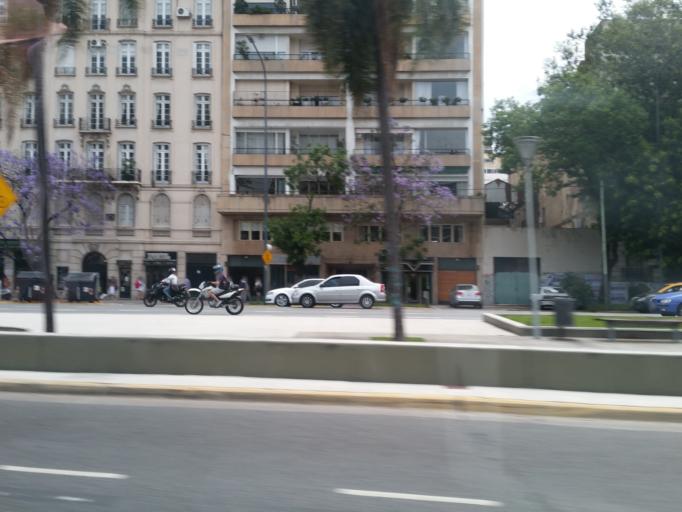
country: AR
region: Buenos Aires F.D.
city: Retiro
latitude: -34.5938
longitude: -58.3825
